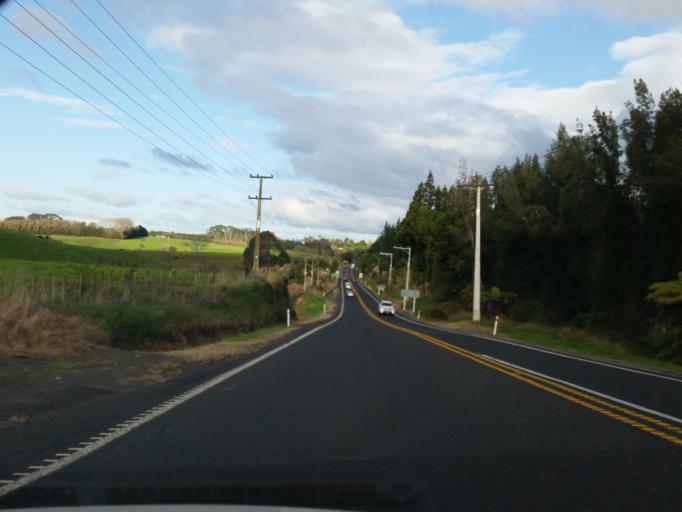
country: NZ
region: Bay of Plenty
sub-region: Tauranga City
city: Tauranga
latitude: -37.6658
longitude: 176.0160
